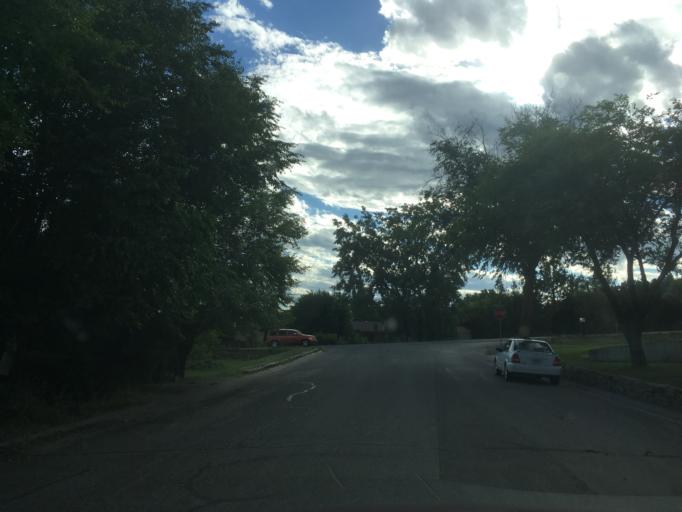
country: US
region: Montana
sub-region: Yellowstone County
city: Billings
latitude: 45.8004
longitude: -108.6012
